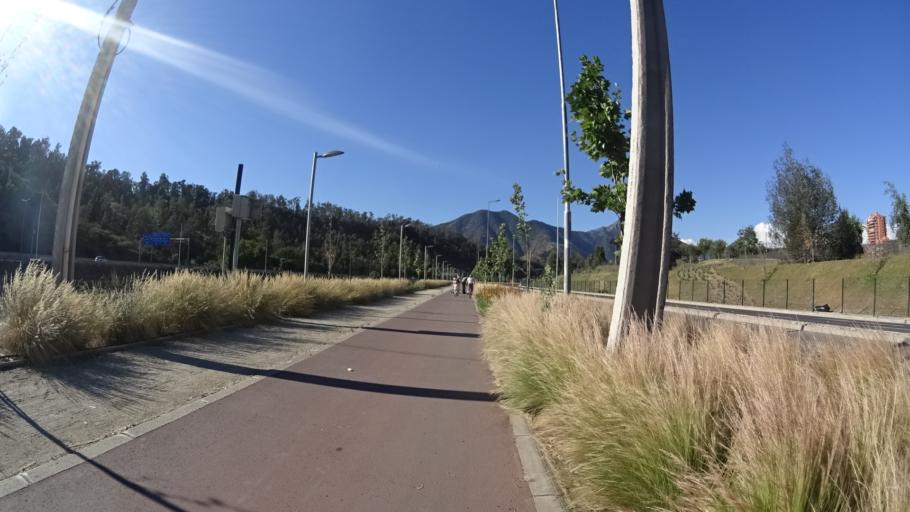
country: CL
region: Santiago Metropolitan
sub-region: Provincia de Santiago
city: Villa Presidente Frei, Nunoa, Santiago, Chile
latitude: -33.3987
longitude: -70.6034
